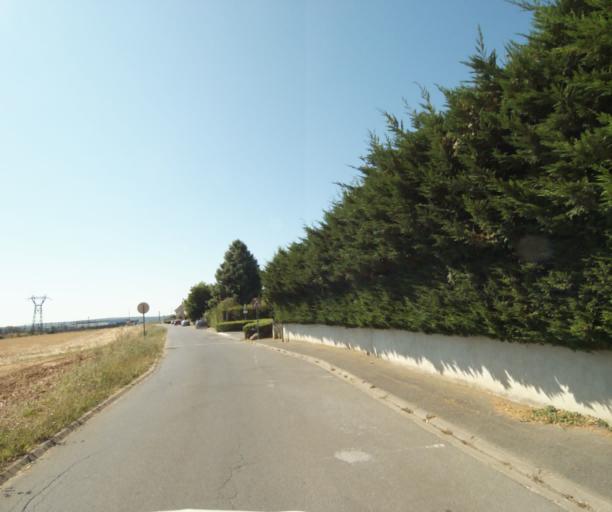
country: FR
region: Ile-de-France
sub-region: Departement de l'Essonne
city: Itteville
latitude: 48.5229
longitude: 2.3535
